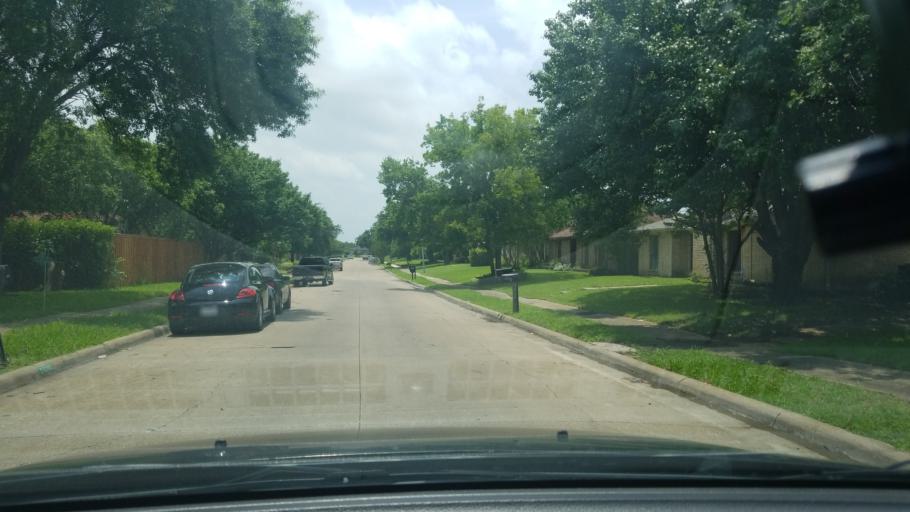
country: US
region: Texas
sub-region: Dallas County
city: Mesquite
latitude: 32.8123
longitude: -96.6082
